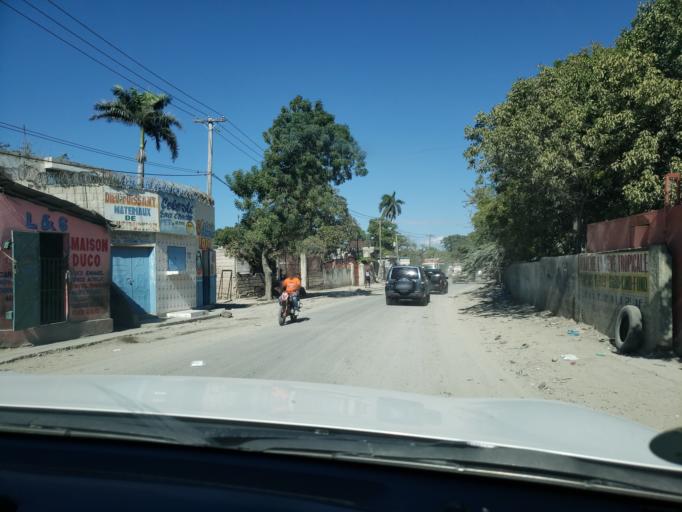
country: HT
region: Ouest
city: Croix des Bouquets
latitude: 18.5739
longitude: -72.2278
